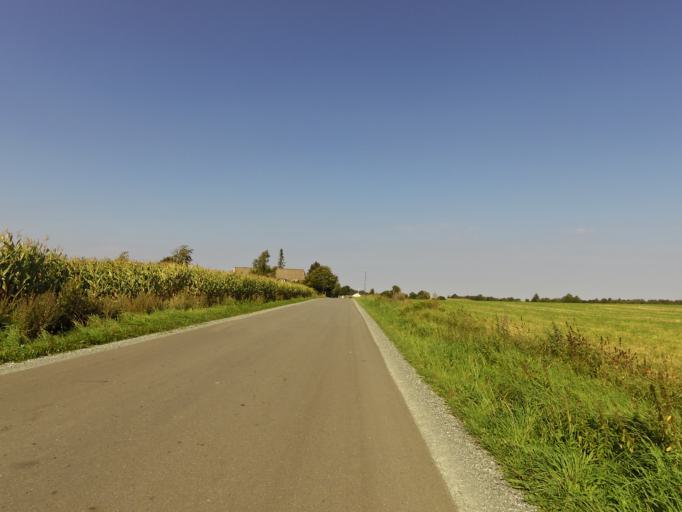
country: DK
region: South Denmark
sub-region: Vejen Kommune
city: Rodding
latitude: 55.3515
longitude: 9.1270
